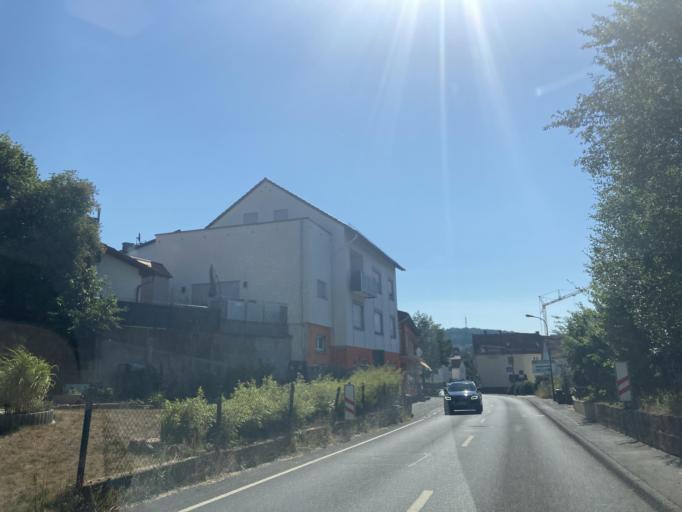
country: DE
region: Hesse
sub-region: Regierungsbezirk Kassel
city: Neuhof
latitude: 50.4569
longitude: 9.6115
